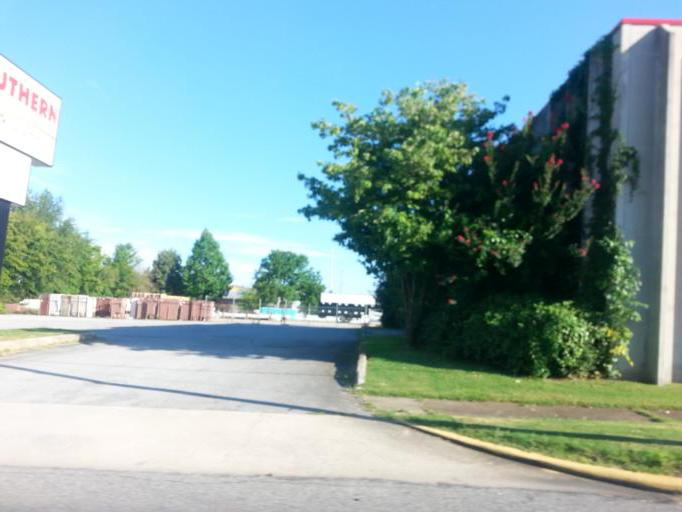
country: US
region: Alabama
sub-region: Lauderdale County
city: Florence
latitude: 34.8026
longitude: -87.6700
